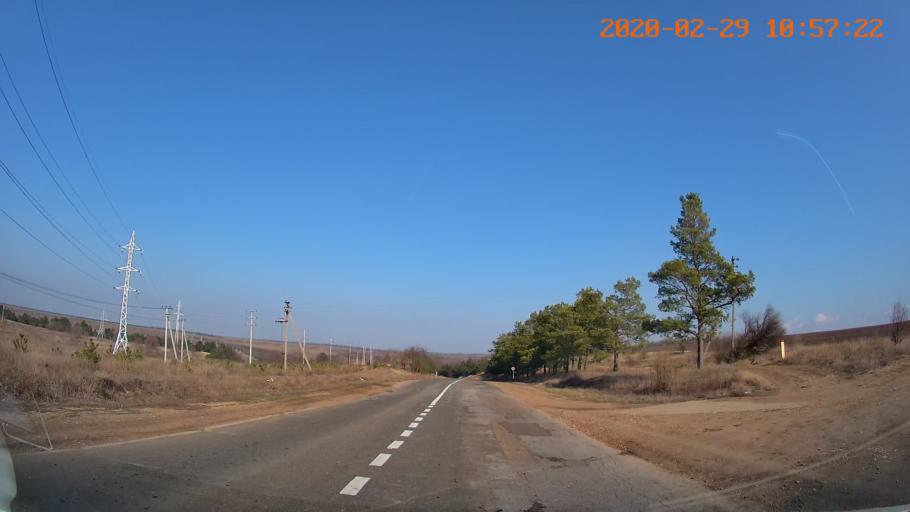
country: MD
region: Telenesti
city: Grigoriopol
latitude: 47.1584
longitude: 29.3218
